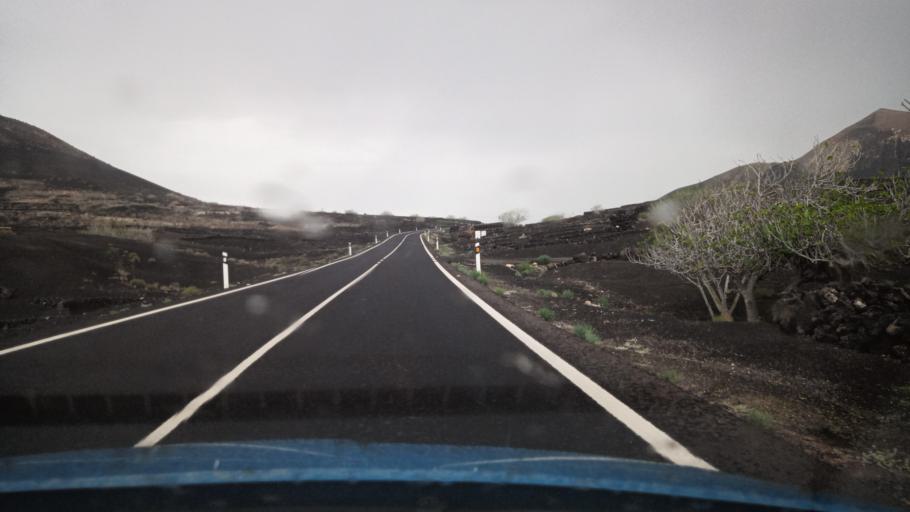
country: ES
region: Canary Islands
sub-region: Provincia de Las Palmas
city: Yaiza
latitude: 28.9624
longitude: -13.7272
